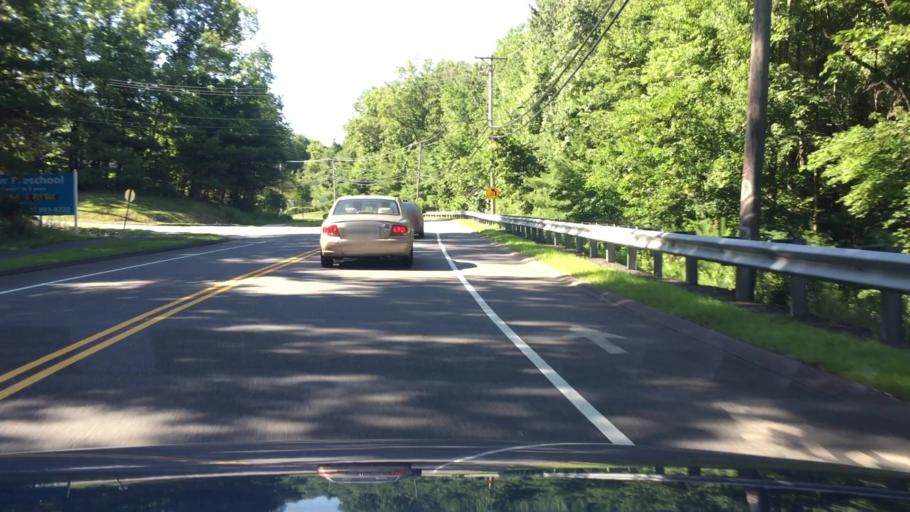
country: US
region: Massachusetts
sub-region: Middlesex County
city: Marlborough
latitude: 42.3299
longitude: -71.5854
